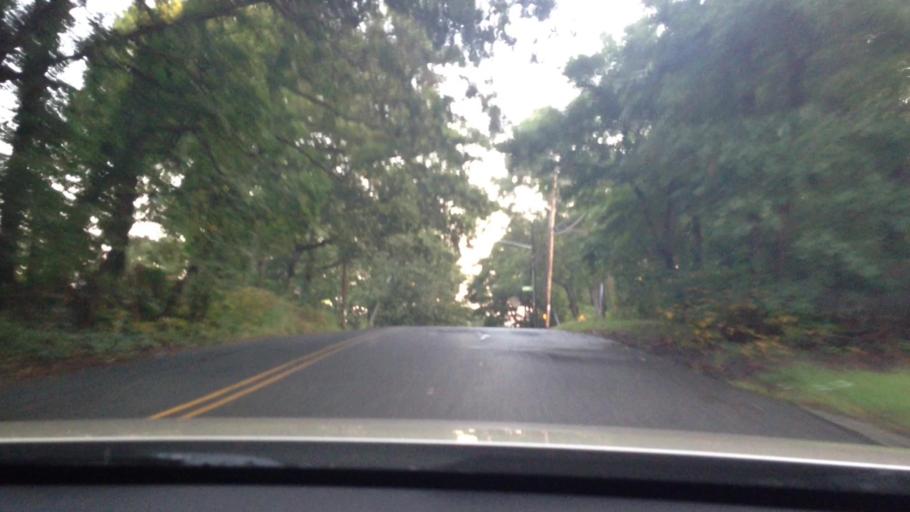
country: US
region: New York
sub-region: Suffolk County
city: Farmingville
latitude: 40.8458
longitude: -73.0352
